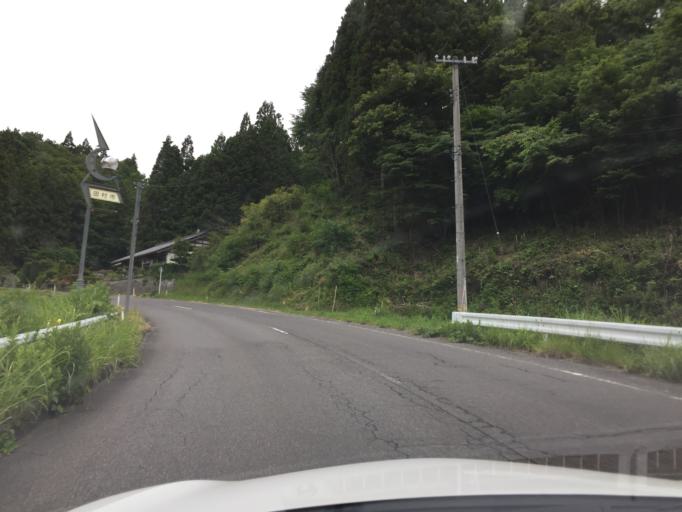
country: JP
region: Fukushima
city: Funehikimachi-funehiki
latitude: 37.3227
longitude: 140.6536
